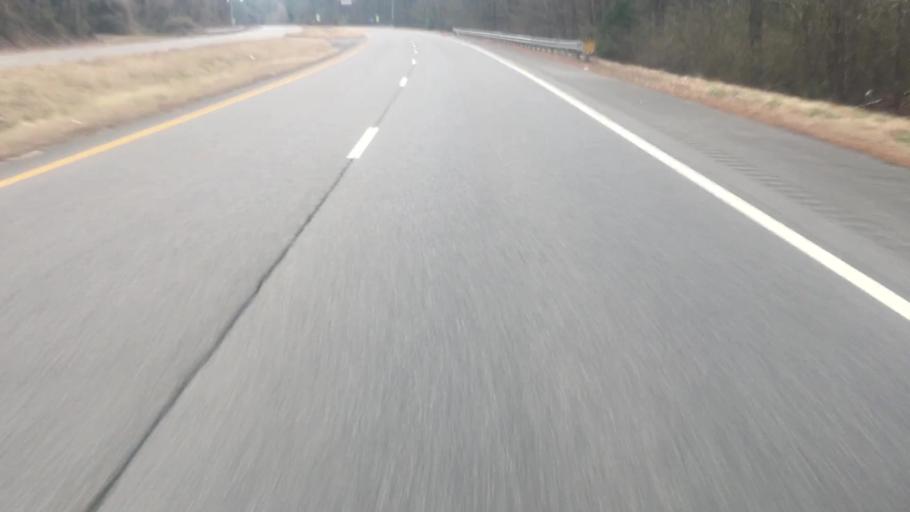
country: US
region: Alabama
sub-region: Walker County
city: Cordova
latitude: 33.8217
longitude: -87.1873
